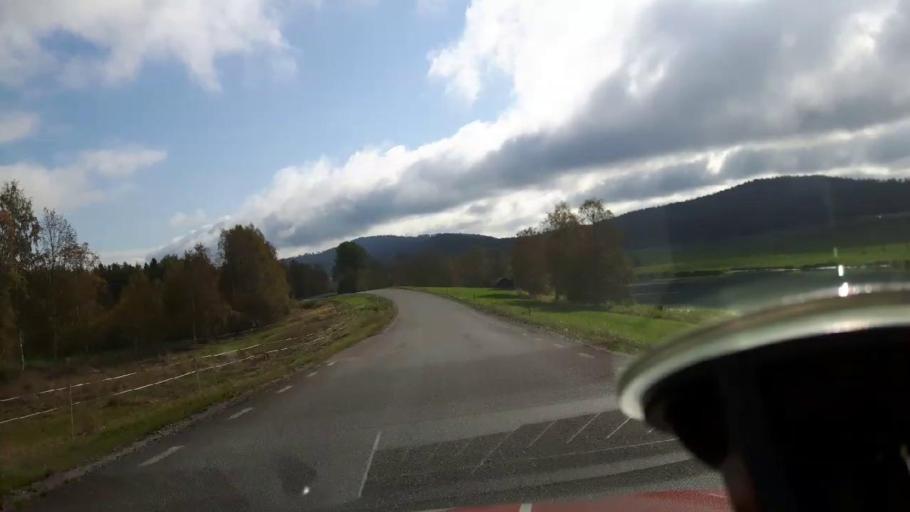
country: SE
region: Gaevleborg
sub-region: Ljusdals Kommun
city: Farila
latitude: 61.7733
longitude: 15.9588
